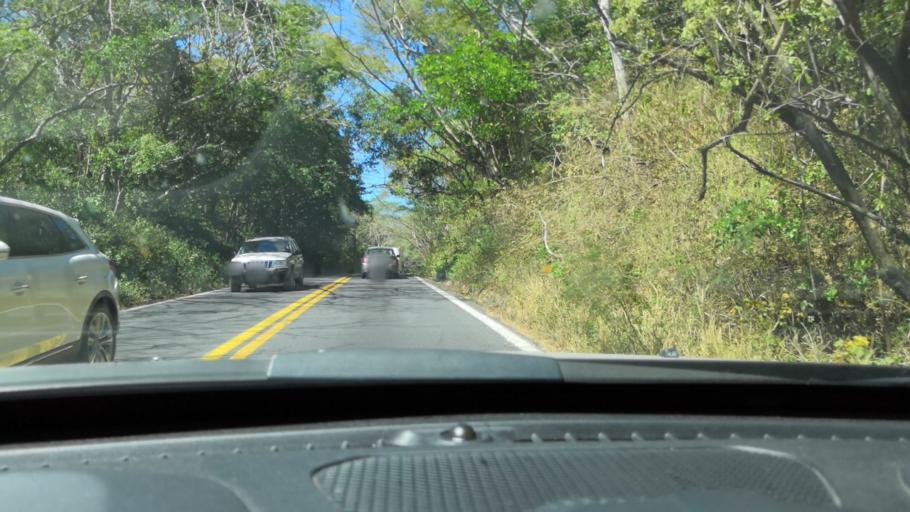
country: MX
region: Nayarit
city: Compostela
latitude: 21.2122
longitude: -104.9890
